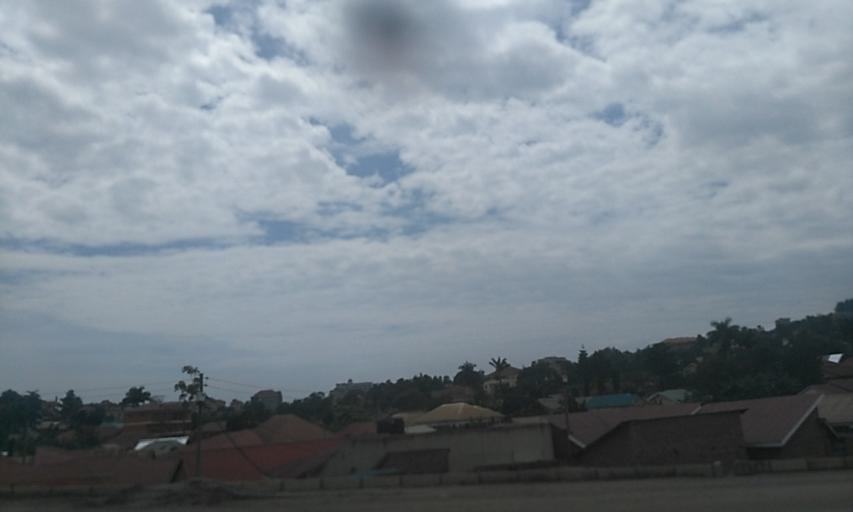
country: UG
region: Central Region
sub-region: Wakiso District
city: Kireka
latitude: 0.3691
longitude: 32.6200
